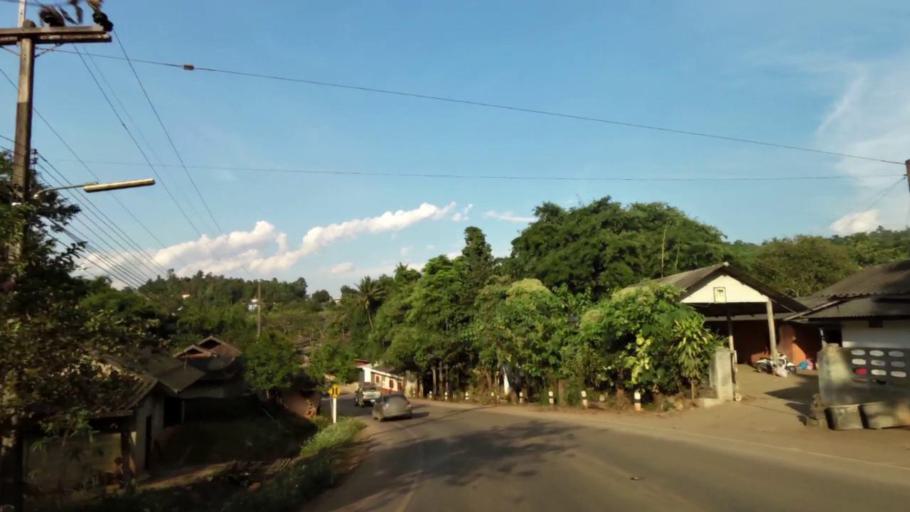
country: TH
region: Chiang Rai
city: Khun Tan
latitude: 19.8651
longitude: 100.3988
